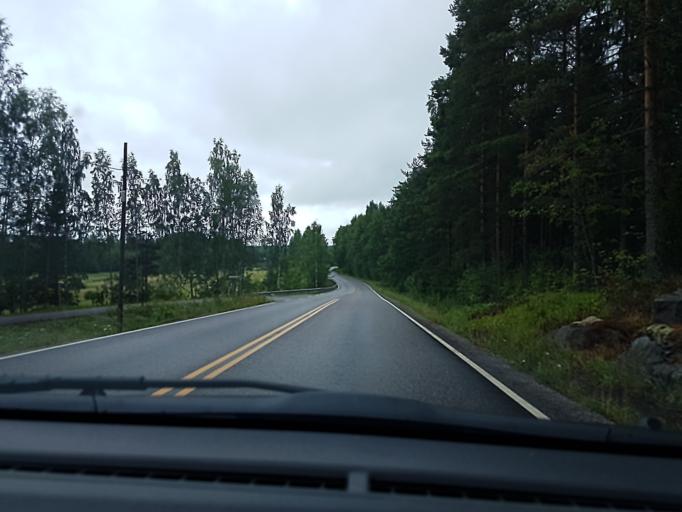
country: FI
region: Uusimaa
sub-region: Helsinki
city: Pornainen
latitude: 60.4564
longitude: 25.3848
